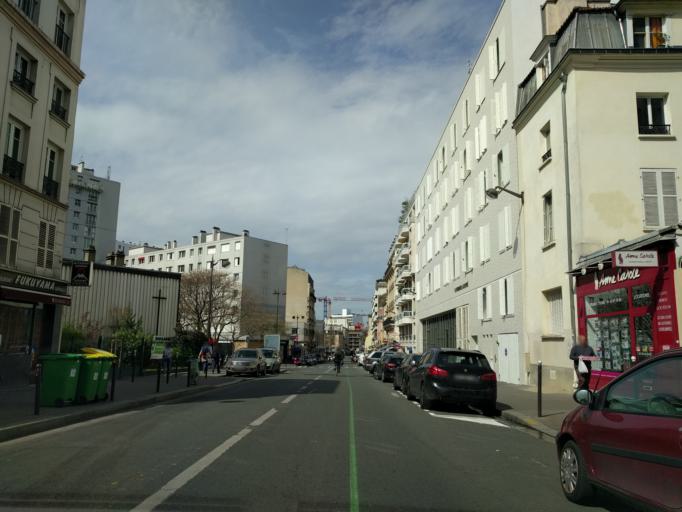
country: FR
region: Ile-de-France
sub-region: Departement du Val-de-Marne
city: Saint-Mande
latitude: 48.8447
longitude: 2.3897
